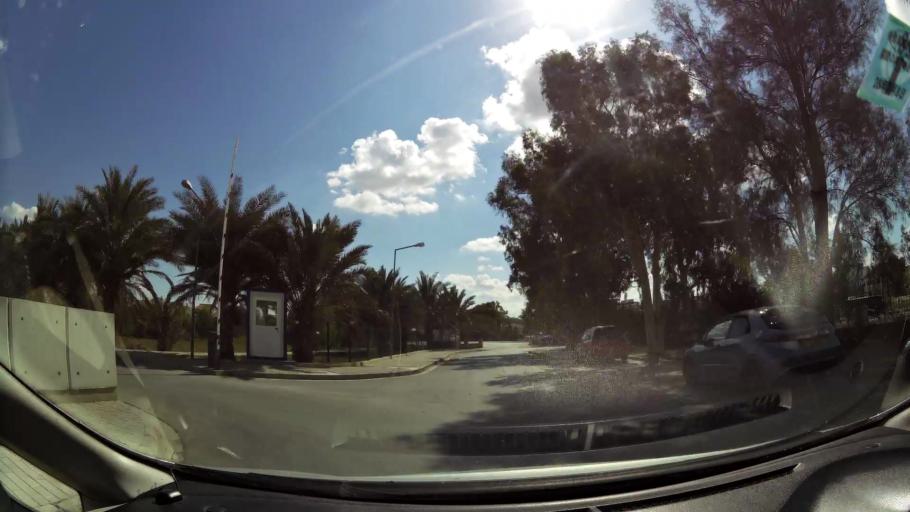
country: CY
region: Lefkosia
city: Nicosia
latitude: 35.2023
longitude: 33.3363
